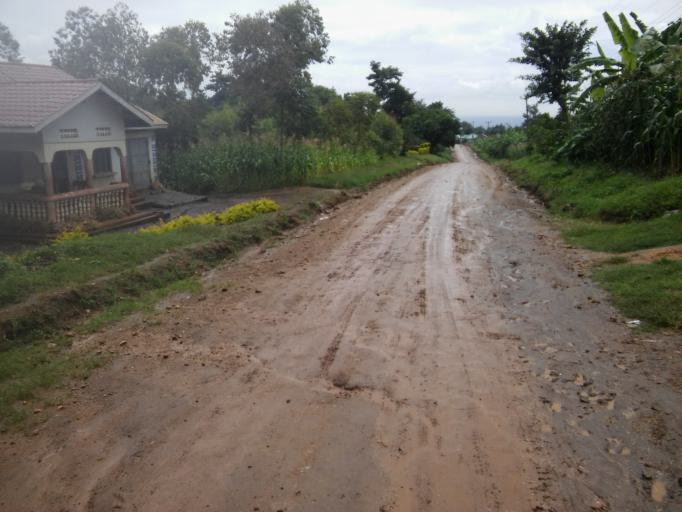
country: UG
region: Eastern Region
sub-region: Mbale District
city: Mbale
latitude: 1.0364
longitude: 34.2092
